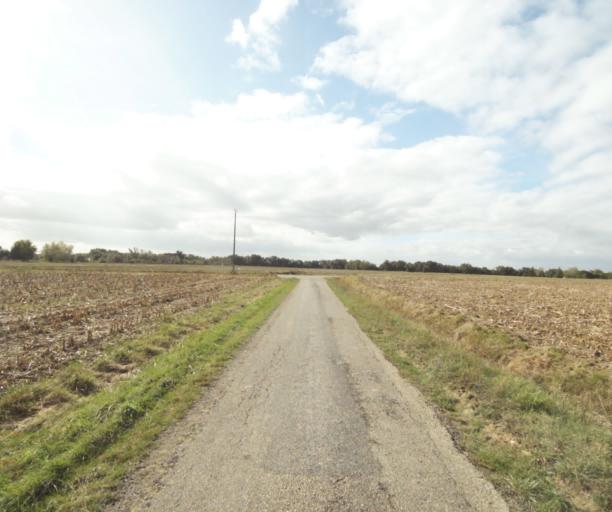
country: FR
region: Midi-Pyrenees
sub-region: Departement du Tarn-et-Garonne
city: Finhan
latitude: 43.9037
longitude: 1.1473
